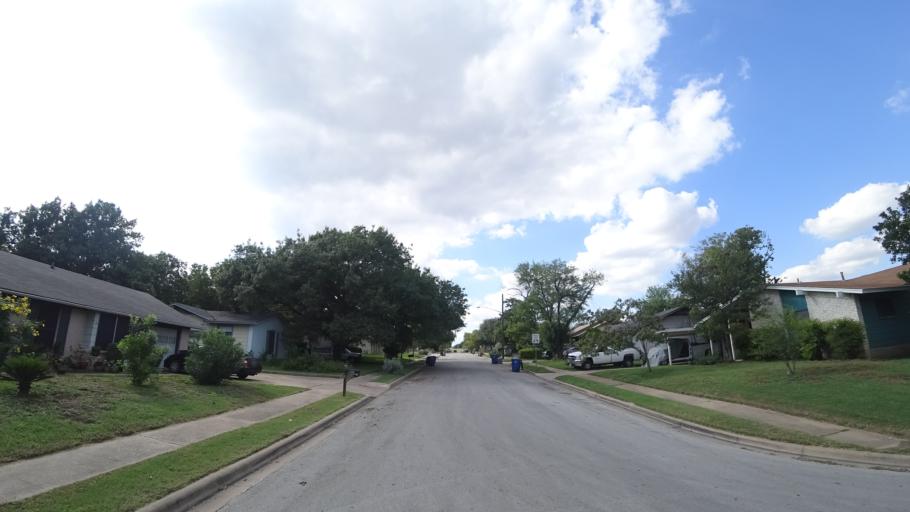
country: US
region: Texas
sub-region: Travis County
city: Wells Branch
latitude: 30.3580
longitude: -97.7021
